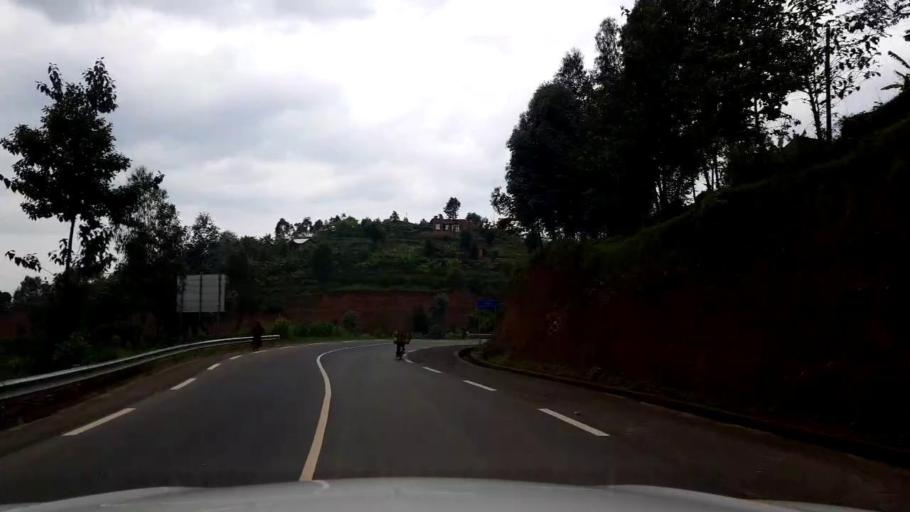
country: RW
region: Western Province
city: Kibuye
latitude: -1.8844
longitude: 29.3472
